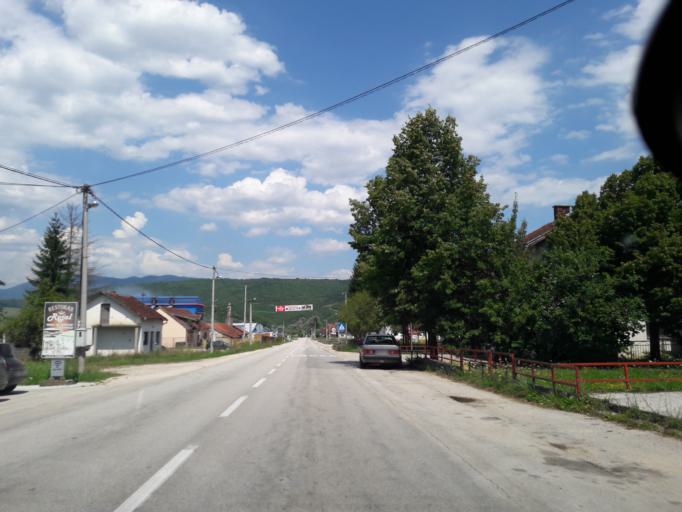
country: BA
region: Republika Srpska
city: Mrkonjic Grad
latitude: 44.4360
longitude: 17.1489
